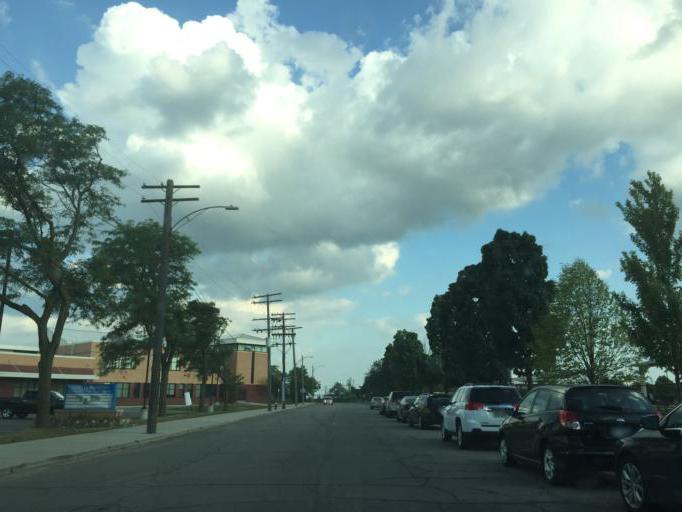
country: US
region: Michigan
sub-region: Wayne County
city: Detroit
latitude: 42.3162
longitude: -83.0906
